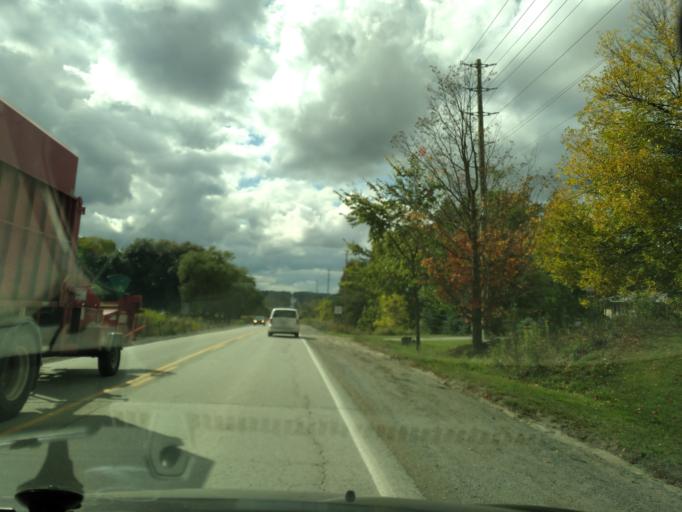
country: CA
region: Ontario
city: Innisfil
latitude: 44.2984
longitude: -79.6207
